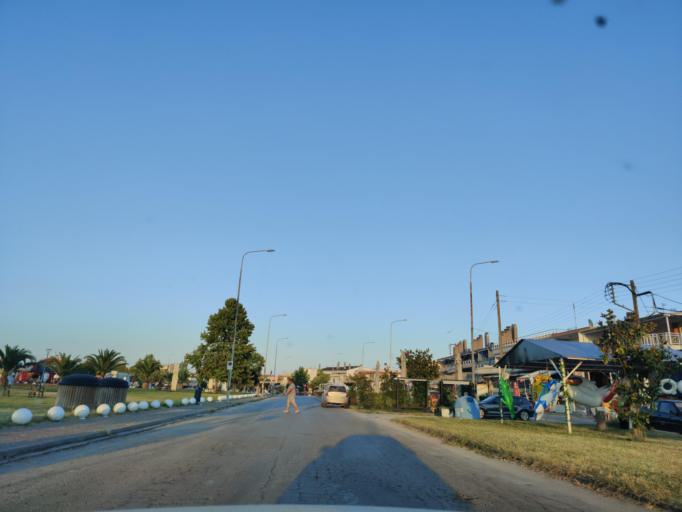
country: GR
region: East Macedonia and Thrace
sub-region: Nomos Kavalas
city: Keramoti
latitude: 40.8563
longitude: 24.6998
